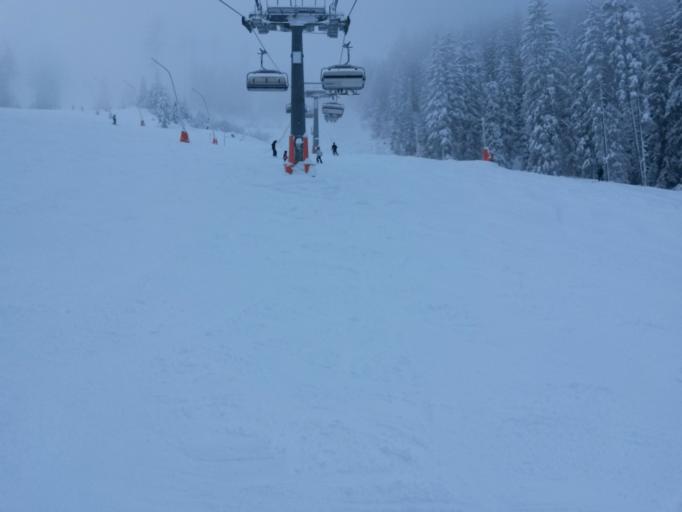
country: AT
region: Salzburg
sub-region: Politischer Bezirk Sankt Johann im Pongau
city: Dorfgastein
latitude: 47.2378
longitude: 13.1770
